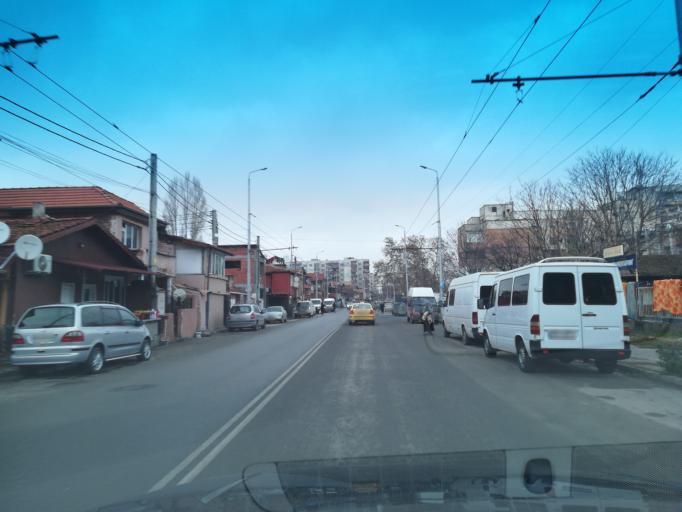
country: BG
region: Plovdiv
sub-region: Obshtina Plovdiv
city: Plovdiv
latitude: 42.1532
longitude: 24.7871
